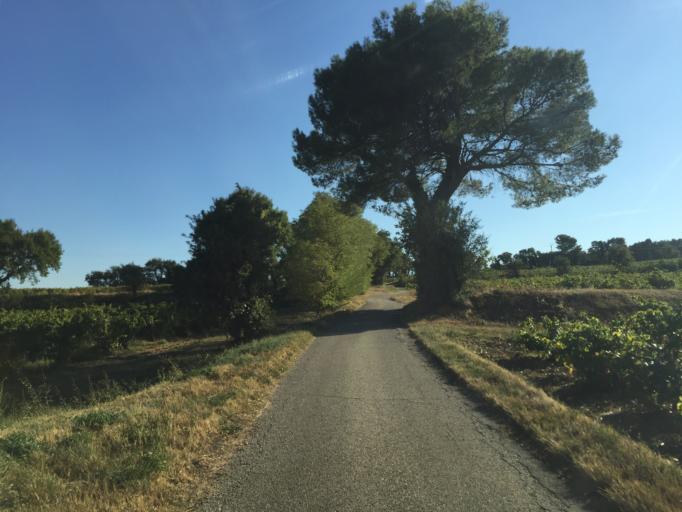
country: FR
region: Provence-Alpes-Cote d'Azur
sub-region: Departement du Vaucluse
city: Courthezon
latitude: 44.0634
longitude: 4.8779
